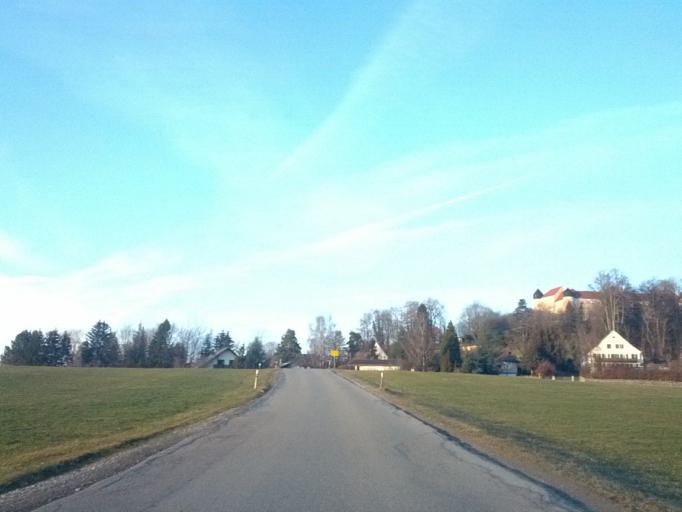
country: DE
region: Bavaria
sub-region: Swabia
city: Kronburg
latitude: 47.9007
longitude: 10.1597
